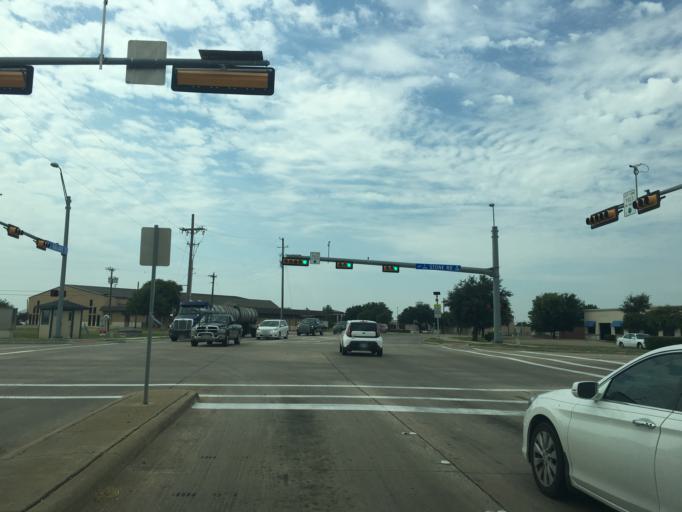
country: US
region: Texas
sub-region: Collin County
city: Wylie
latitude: 33.0065
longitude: -96.5391
